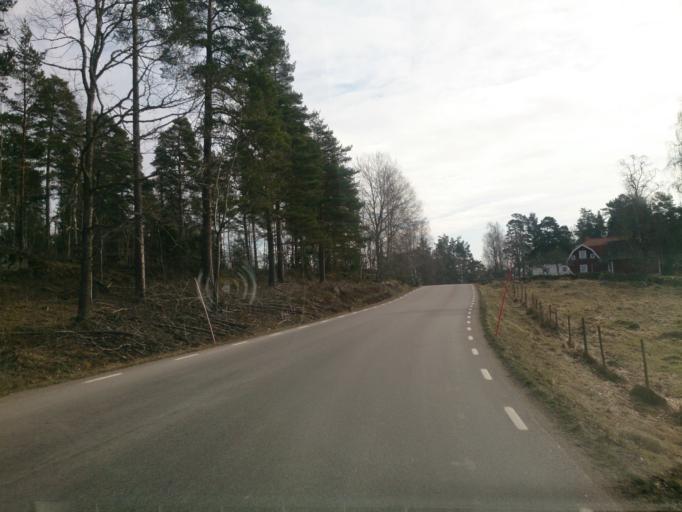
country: SE
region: OEstergoetland
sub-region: Linkopings Kommun
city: Sturefors
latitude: 58.2960
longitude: 15.8740
